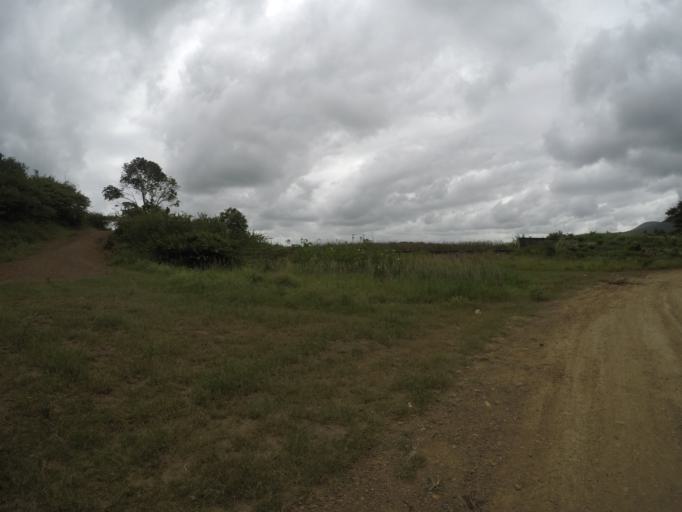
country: ZA
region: KwaZulu-Natal
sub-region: uThungulu District Municipality
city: Empangeni
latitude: -28.5635
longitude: 31.8667
